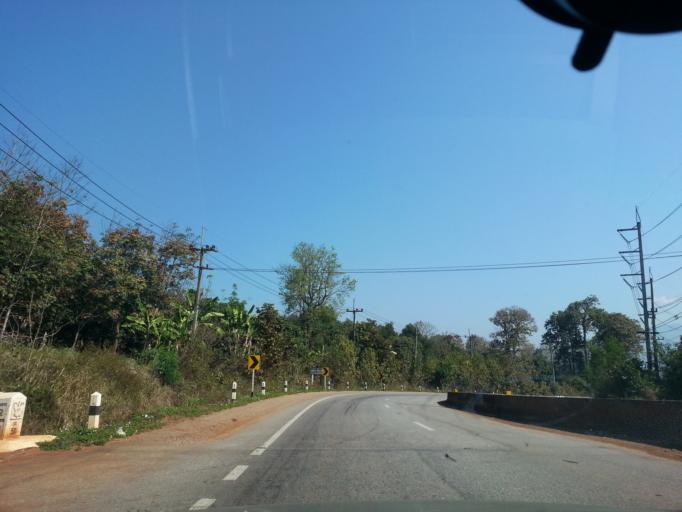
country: TH
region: Chiang Mai
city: Mae Taeng
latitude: 19.2028
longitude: 98.9654
